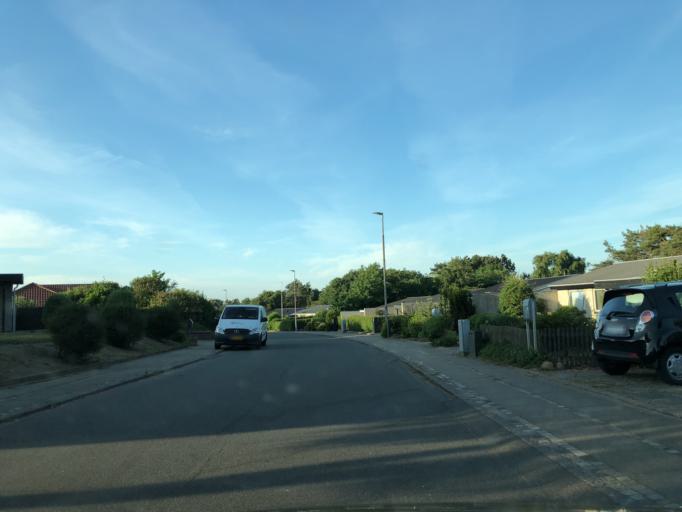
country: DK
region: Central Jutland
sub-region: Struer Kommune
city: Struer
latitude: 56.4847
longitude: 8.5874
